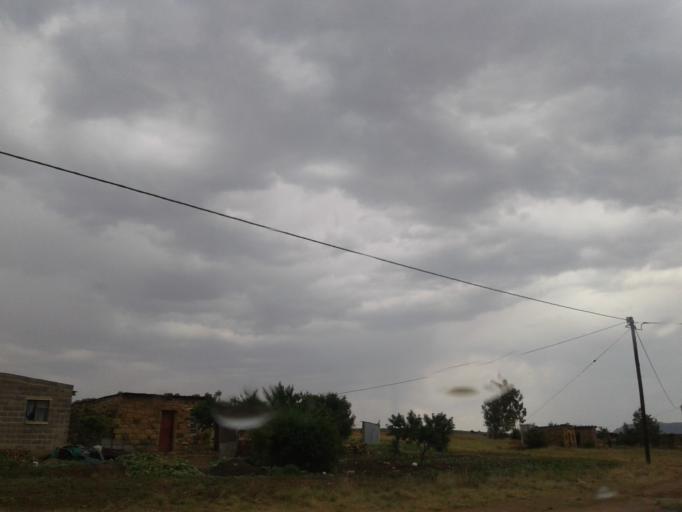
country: LS
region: Quthing
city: Quthing
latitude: -30.3638
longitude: 27.5478
